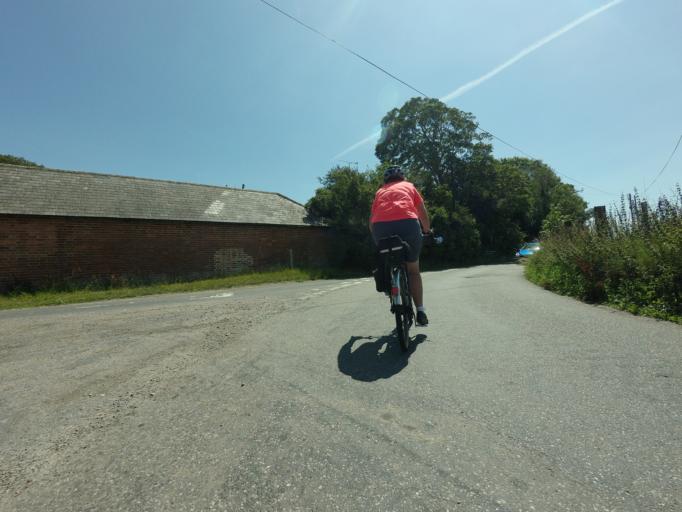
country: GB
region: England
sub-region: Kent
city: Lydd
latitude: 50.9595
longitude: 0.9032
